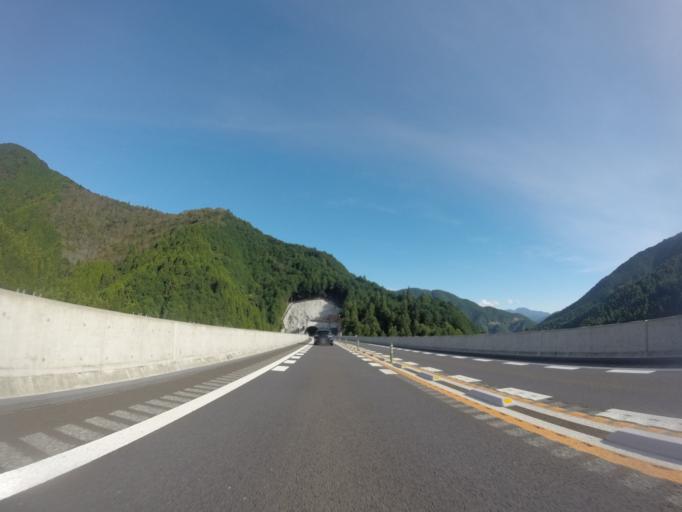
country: JP
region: Shizuoka
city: Fujinomiya
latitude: 35.2016
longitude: 138.4607
